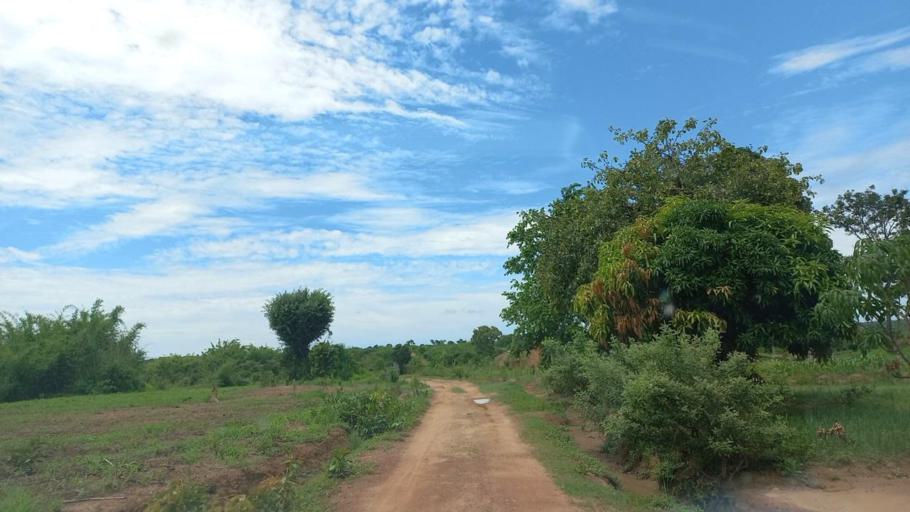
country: ZM
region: Copperbelt
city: Kitwe
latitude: -12.8146
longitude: 28.3914
